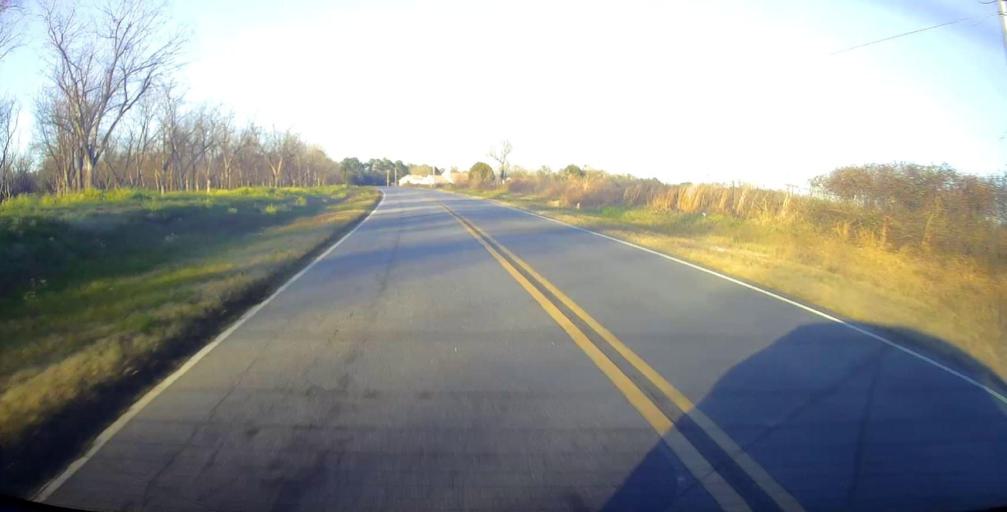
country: US
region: Georgia
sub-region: Dougherty County
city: Albany
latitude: 31.5190
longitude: -84.2305
